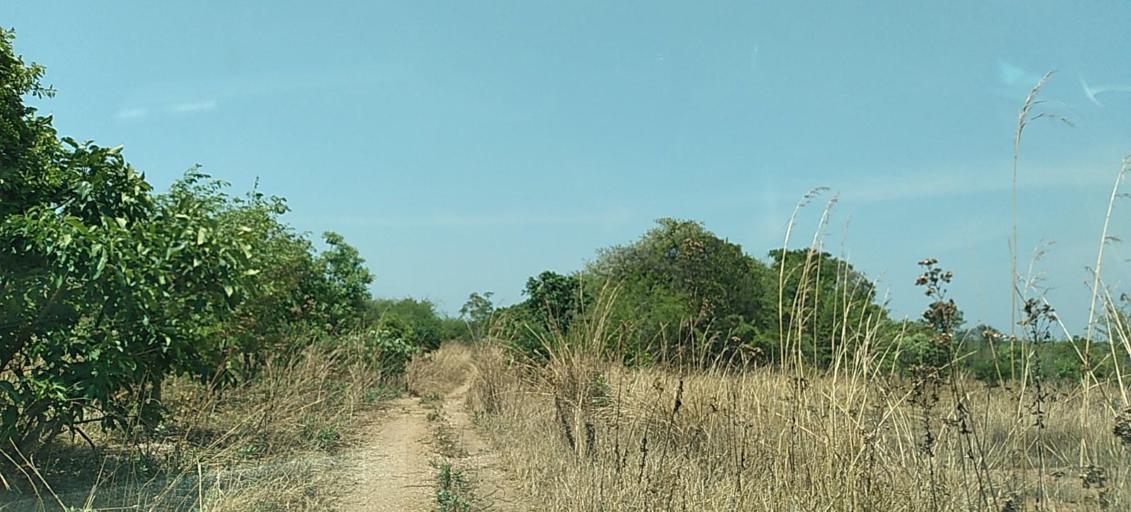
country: ZM
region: Copperbelt
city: Luanshya
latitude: -12.9852
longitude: 28.3273
